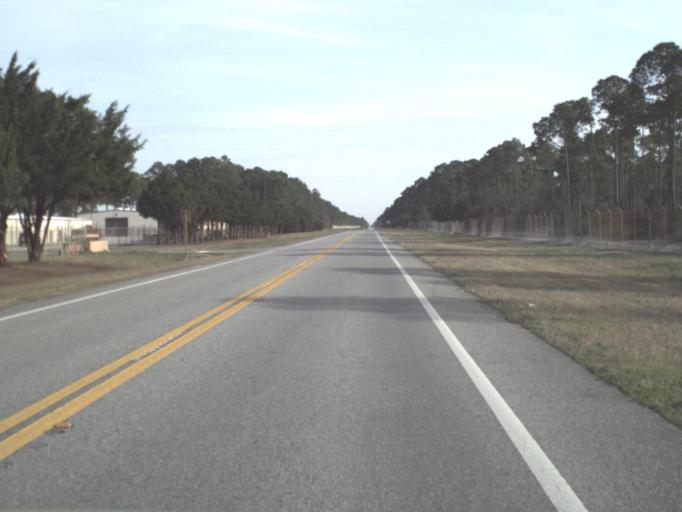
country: US
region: Florida
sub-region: Bay County
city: Tyndall Air Force Base
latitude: 30.0624
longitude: -85.5804
